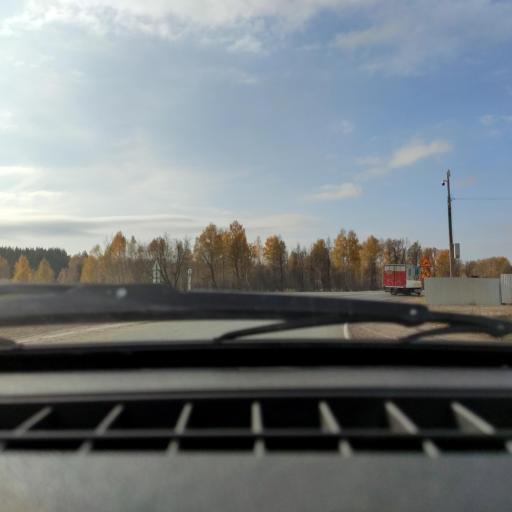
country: RU
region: Bashkortostan
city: Iglino
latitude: 54.7424
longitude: 56.3015
